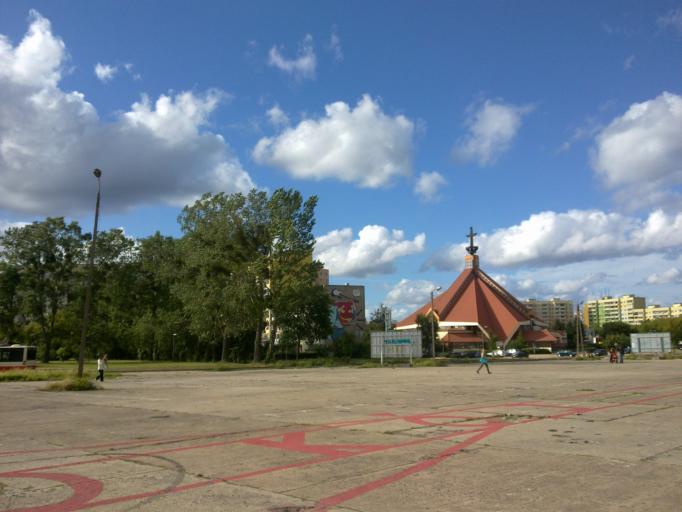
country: PL
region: Pomeranian Voivodeship
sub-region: Gdansk
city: Gdansk
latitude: 54.3896
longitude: 18.5966
